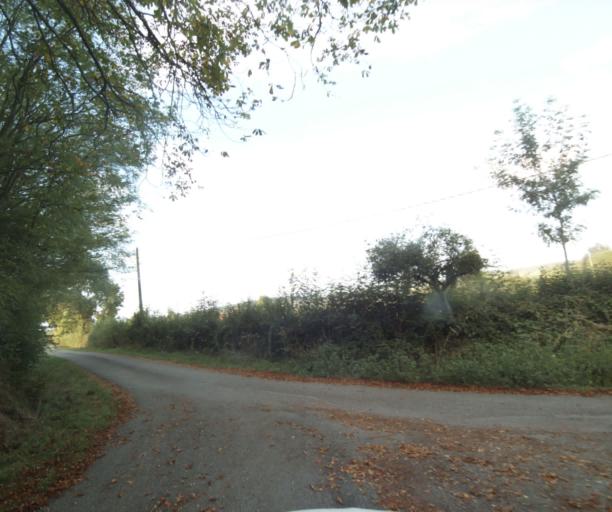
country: FR
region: Bourgogne
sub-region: Departement de Saone-et-Loire
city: Charolles
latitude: 46.4382
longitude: 4.3632
